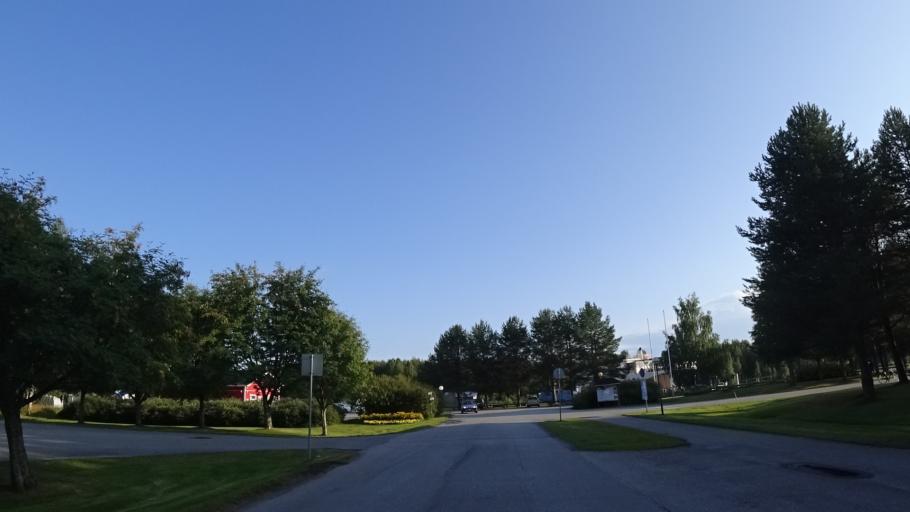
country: FI
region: North Karelia
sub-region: Pielisen Karjala
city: Lieksa
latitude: 63.3092
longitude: 30.0129
